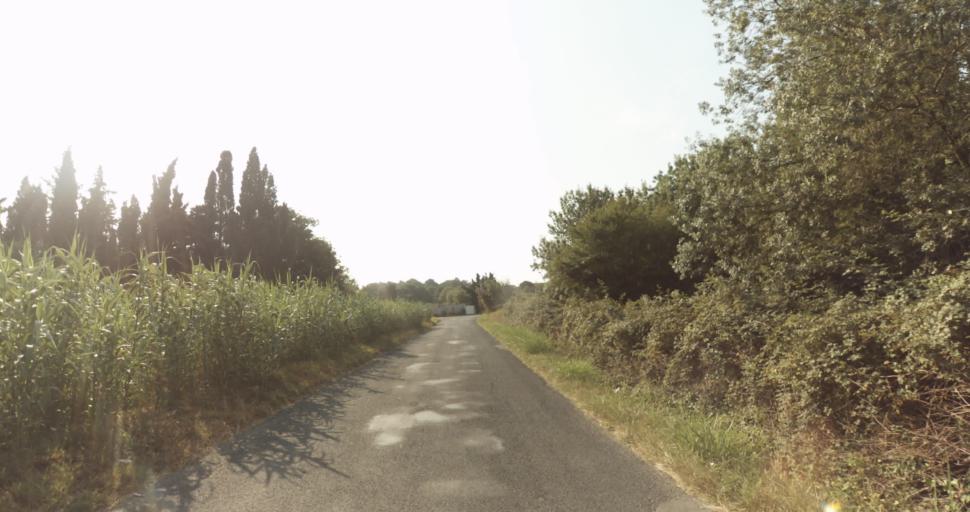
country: FR
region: Languedoc-Roussillon
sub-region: Departement des Pyrenees-Orientales
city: Latour-Bas-Elne
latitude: 42.6144
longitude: 2.9877
